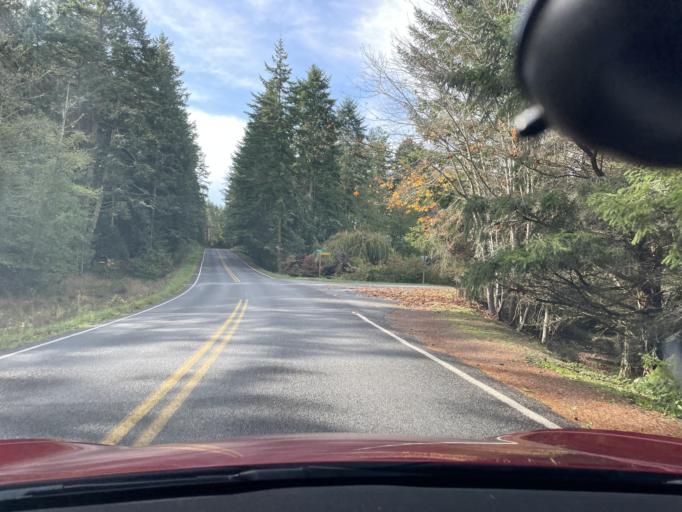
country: US
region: Washington
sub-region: San Juan County
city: Friday Harbor
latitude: 48.5282
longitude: -122.9913
